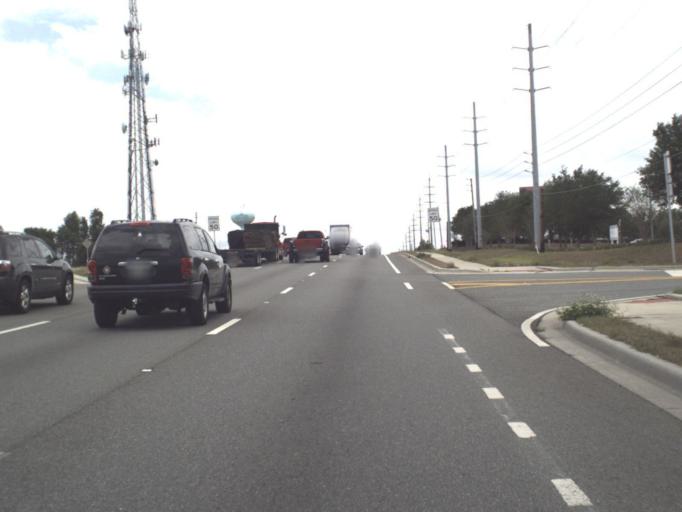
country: US
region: Florida
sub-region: Lake County
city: Minneola
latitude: 28.5467
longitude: -81.7218
